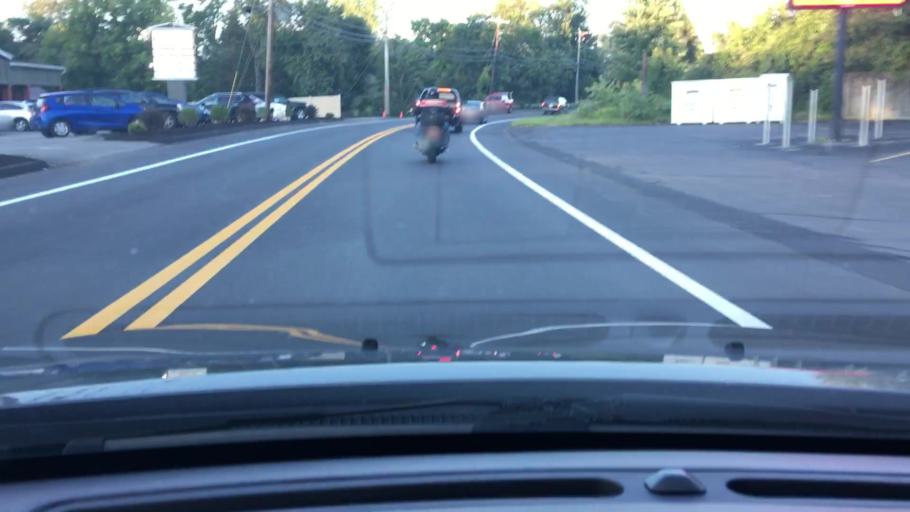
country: US
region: Massachusetts
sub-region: Worcester County
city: Grafton
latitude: 42.2299
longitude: -71.7175
